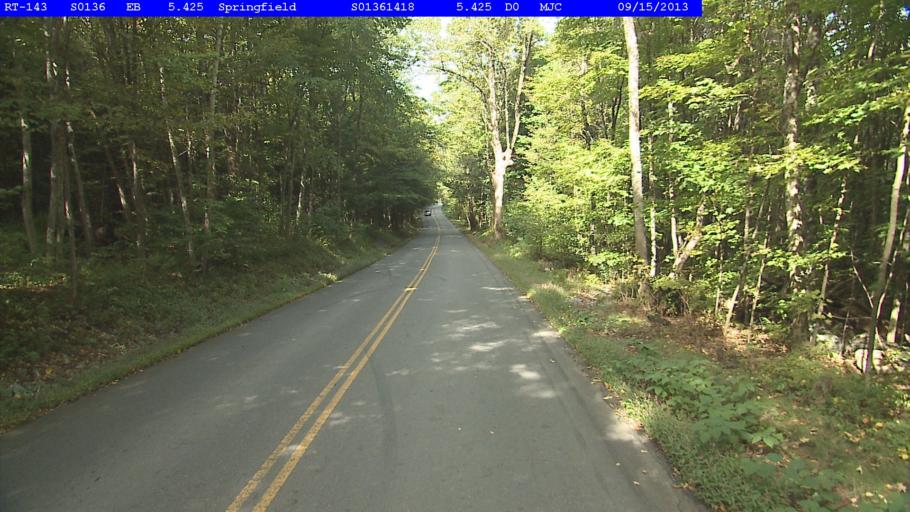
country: US
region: Vermont
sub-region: Windsor County
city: Springfield
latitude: 43.3268
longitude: -72.4123
